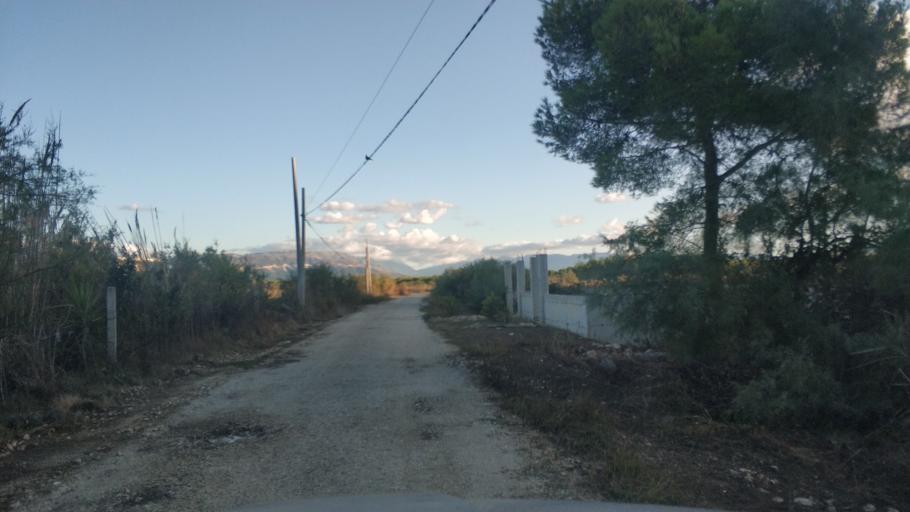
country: AL
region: Vlore
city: Vlore
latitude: 40.5090
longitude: 19.4227
